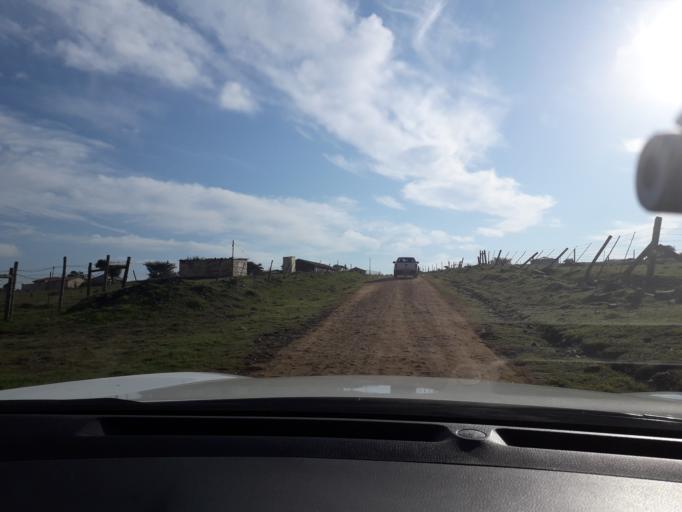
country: ZA
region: Eastern Cape
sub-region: Buffalo City Metropolitan Municipality
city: Bhisho
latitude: -32.9395
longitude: 27.2899
